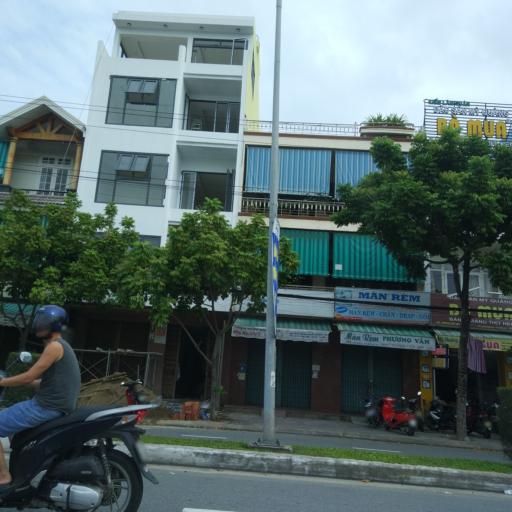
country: VN
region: Da Nang
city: Son Tra
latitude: 16.0690
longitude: 108.2321
